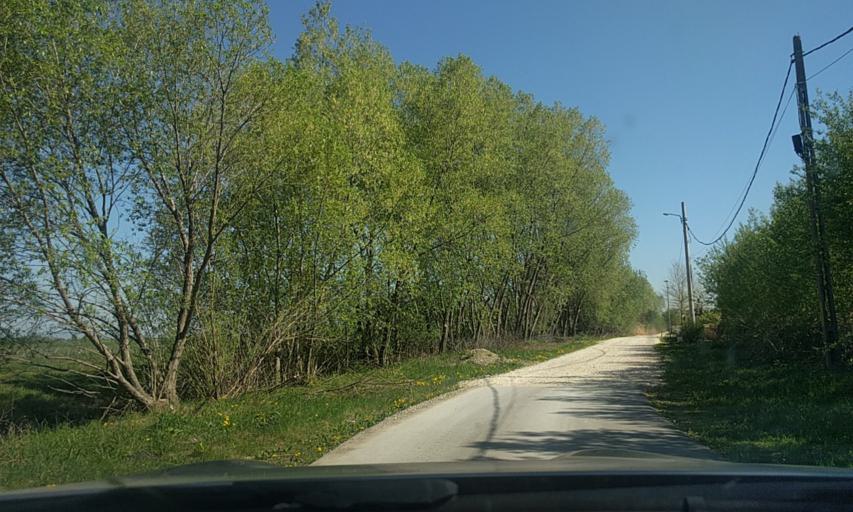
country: RO
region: Brasov
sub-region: Comuna Bod
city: Colonia Bod
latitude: 45.7199
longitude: 25.5663
